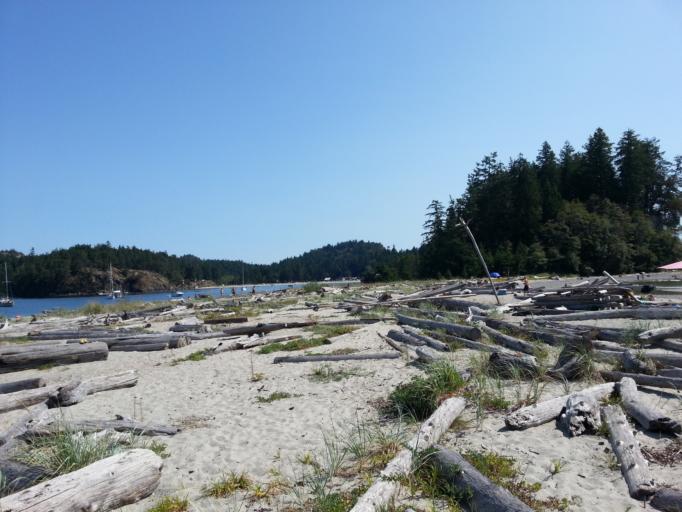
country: CA
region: British Columbia
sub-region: Sunshine Coast Regional District
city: Sechelt
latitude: 49.4945
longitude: -123.9901
